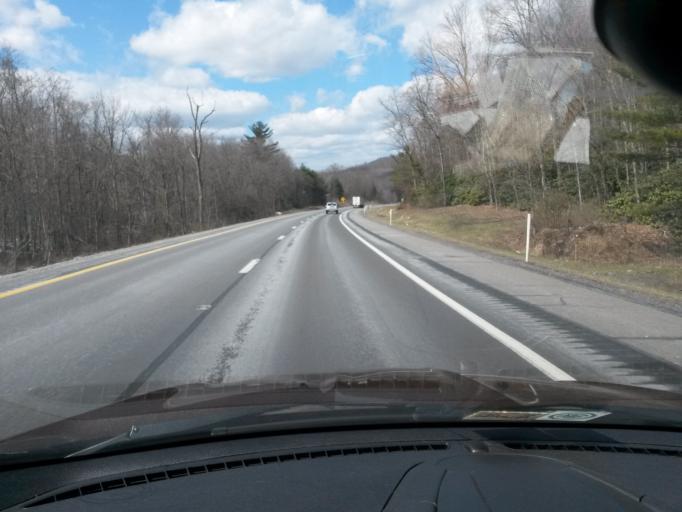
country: US
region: West Virginia
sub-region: Raleigh County
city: Shady Spring
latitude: 37.6876
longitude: -81.1282
